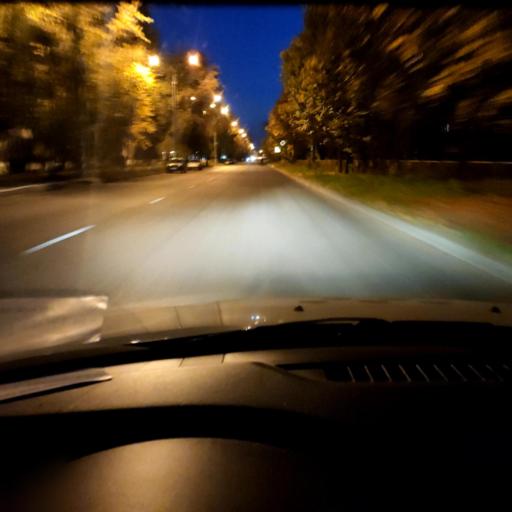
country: RU
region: Samara
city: Tol'yatti
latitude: 53.5243
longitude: 49.4283
